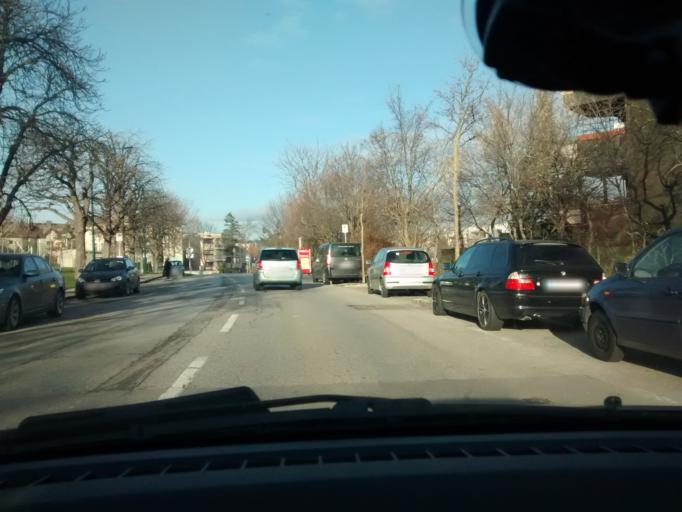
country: AT
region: Lower Austria
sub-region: Politischer Bezirk Modling
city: Modling
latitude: 48.0736
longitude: 16.2939
